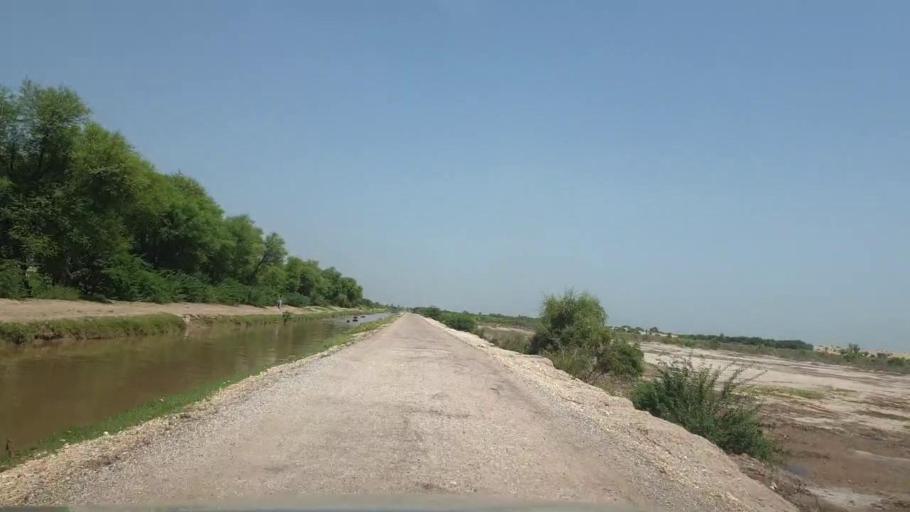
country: PK
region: Sindh
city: Rohri
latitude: 27.6183
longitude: 69.0987
